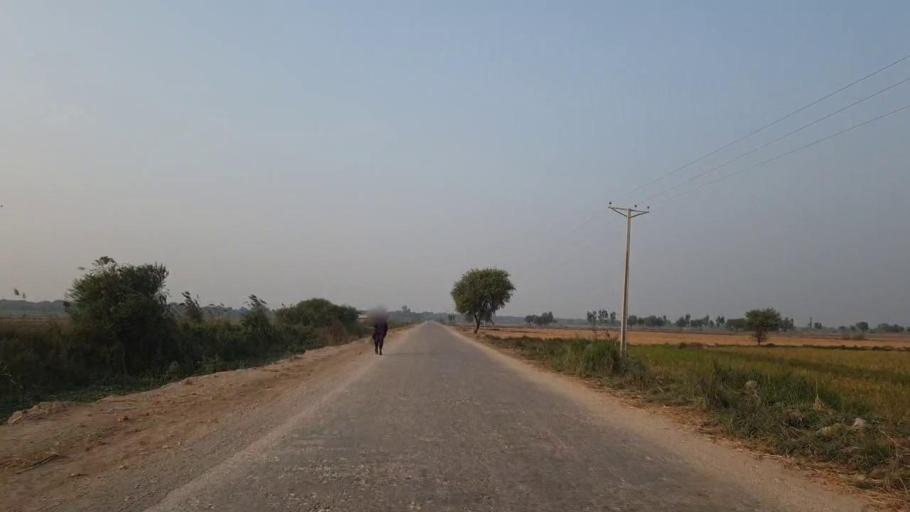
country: PK
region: Sindh
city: Tando Muhammad Khan
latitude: 25.1071
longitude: 68.4300
